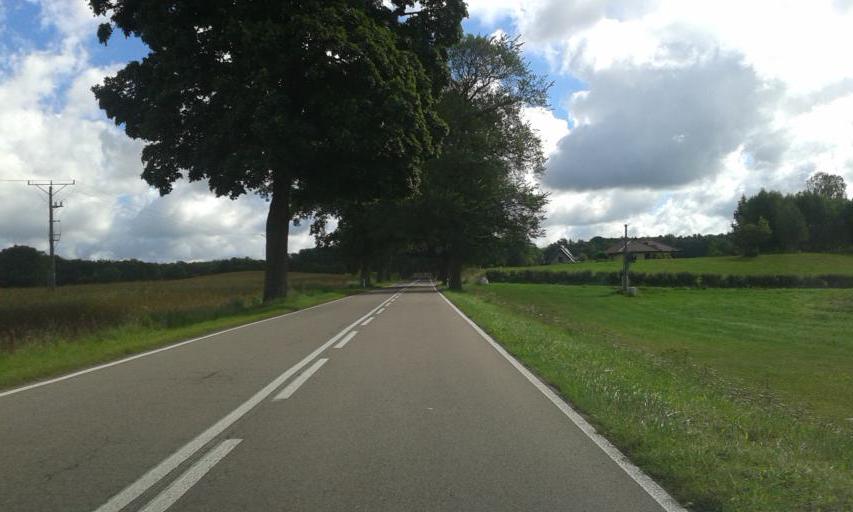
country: PL
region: West Pomeranian Voivodeship
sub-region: Powiat koszalinski
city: Bobolice
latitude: 53.9658
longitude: 16.6282
